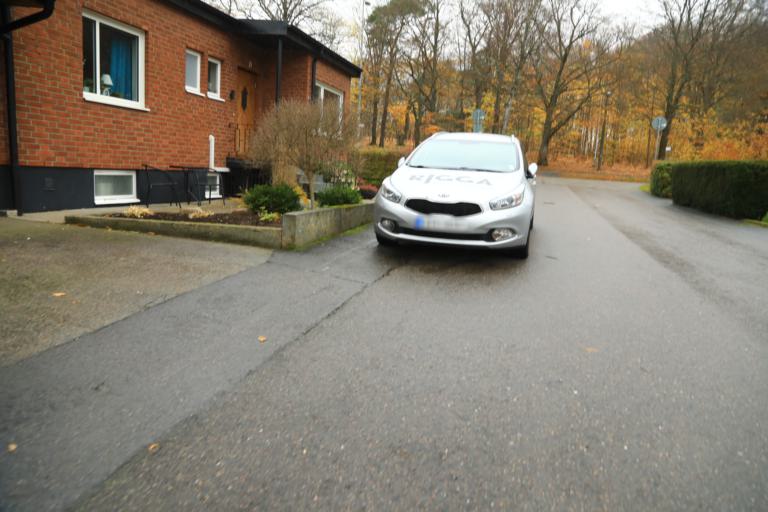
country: SE
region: Halland
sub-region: Varbergs Kommun
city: Varberg
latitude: 57.0999
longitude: 12.2608
